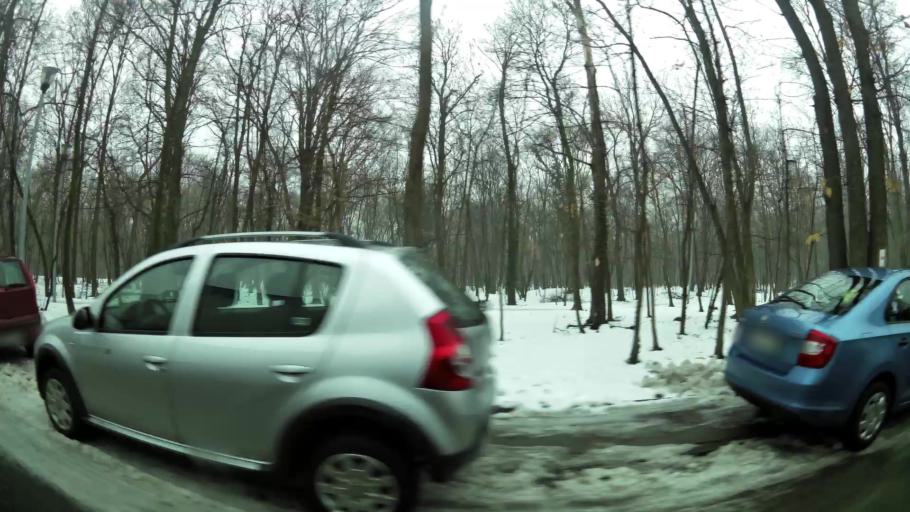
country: RS
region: Central Serbia
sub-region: Belgrade
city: Savski Venac
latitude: 44.7855
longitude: 20.4443
